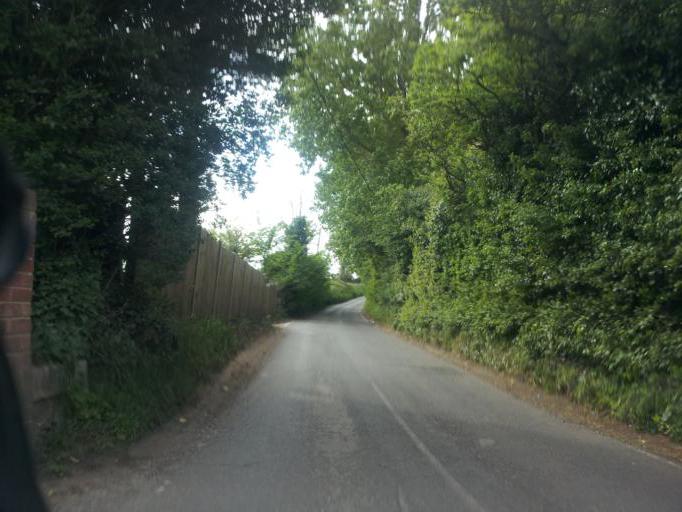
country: GB
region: England
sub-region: Kent
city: Teynham
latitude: 51.3310
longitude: 0.8146
